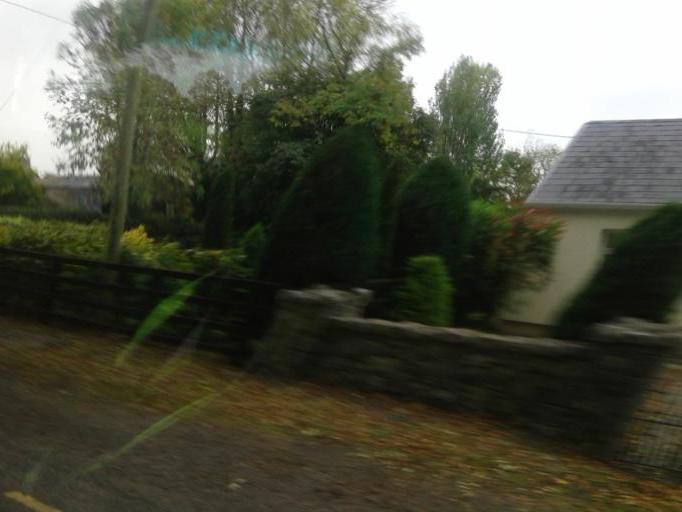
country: IE
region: Munster
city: Nenagh Bridge
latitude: 52.9493
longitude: -8.0346
